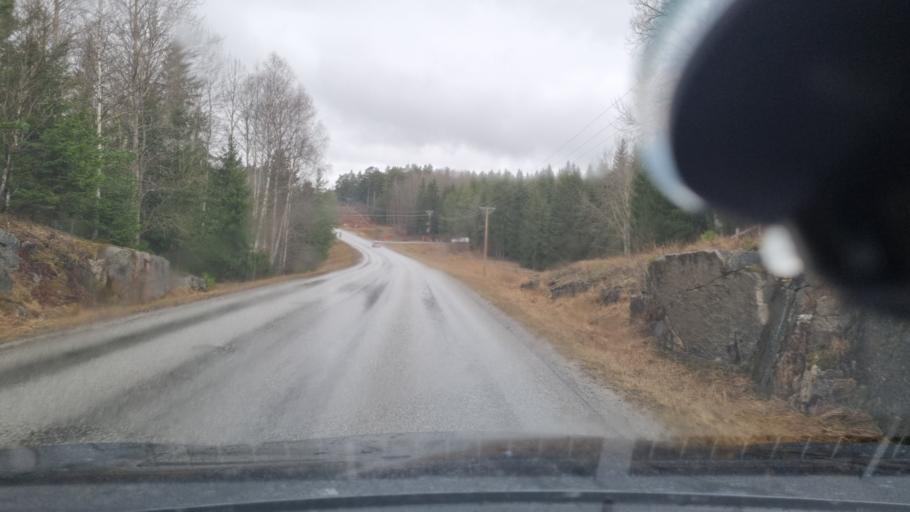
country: SE
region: Stockholm
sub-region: Sigtuna Kommun
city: Sigtuna
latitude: 59.5567
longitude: 17.7217
